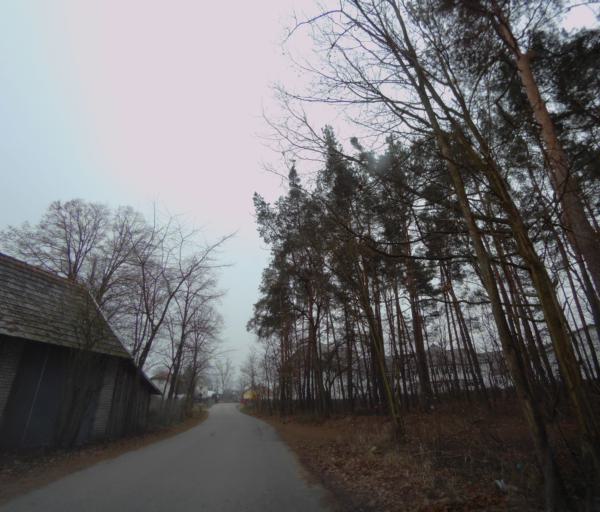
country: PL
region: Subcarpathian Voivodeship
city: Nowa Sarzyna
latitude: 50.2970
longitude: 22.3512
